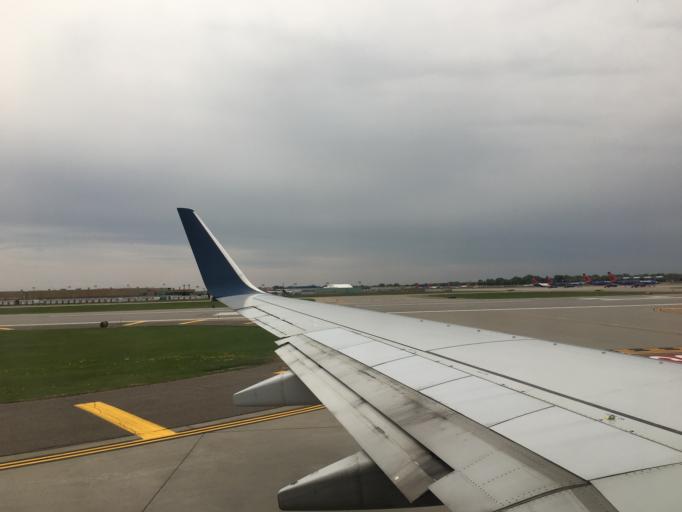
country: US
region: Minnesota
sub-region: Hennepin County
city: Richfield
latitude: 44.8880
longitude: -93.2315
